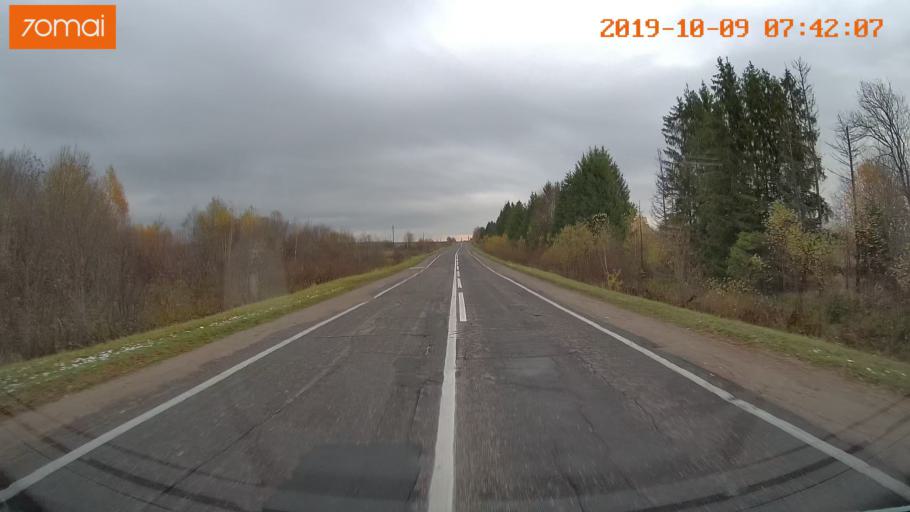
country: RU
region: Jaroslavl
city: Kukoboy
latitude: 58.6416
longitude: 39.7170
